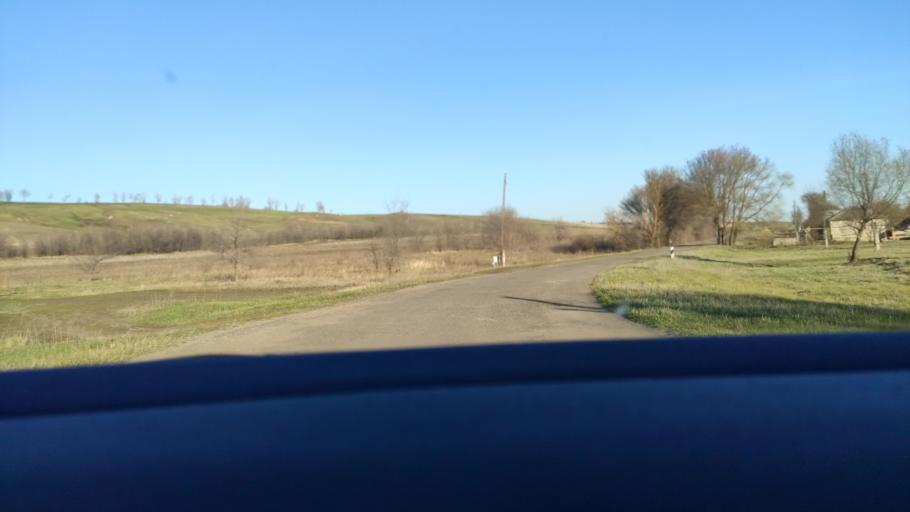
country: RU
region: Voronezj
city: Uryv-Pokrovka
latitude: 51.1478
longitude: 39.0294
